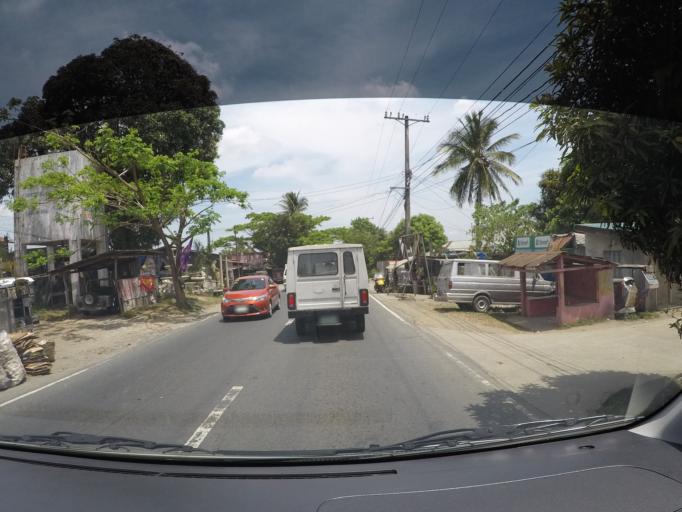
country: PH
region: Calabarzon
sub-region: Province of Cavite
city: Lumil
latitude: 14.1946
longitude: 121.0189
